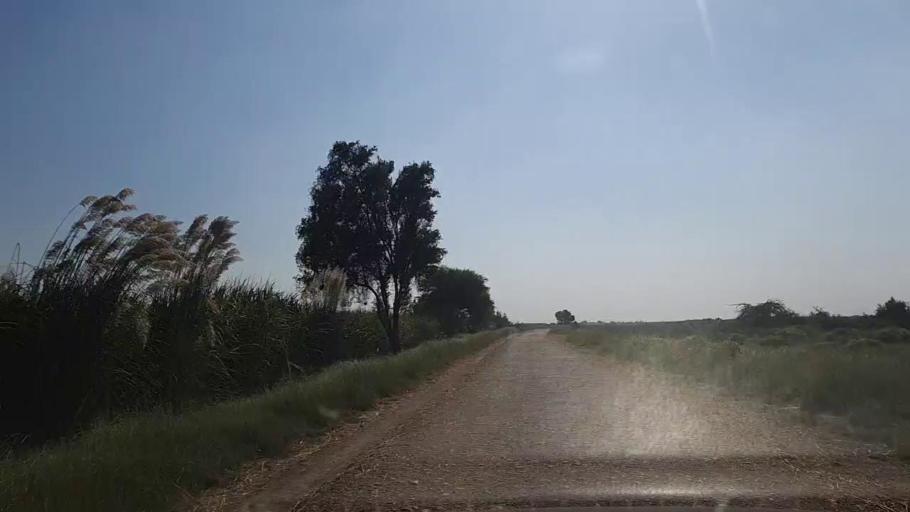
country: PK
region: Sindh
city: Daro Mehar
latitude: 24.7664
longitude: 68.0683
